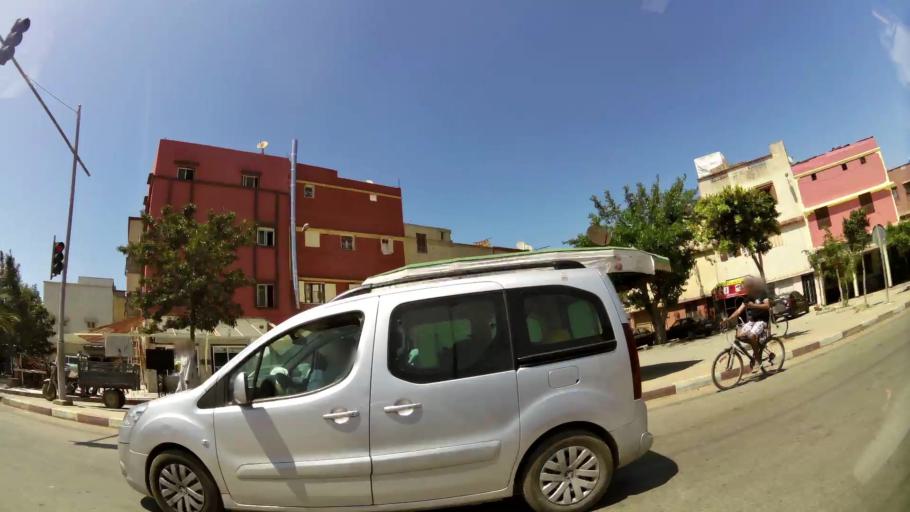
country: MA
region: Gharb-Chrarda-Beni Hssen
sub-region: Kenitra Province
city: Kenitra
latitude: 34.2448
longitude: -6.5511
